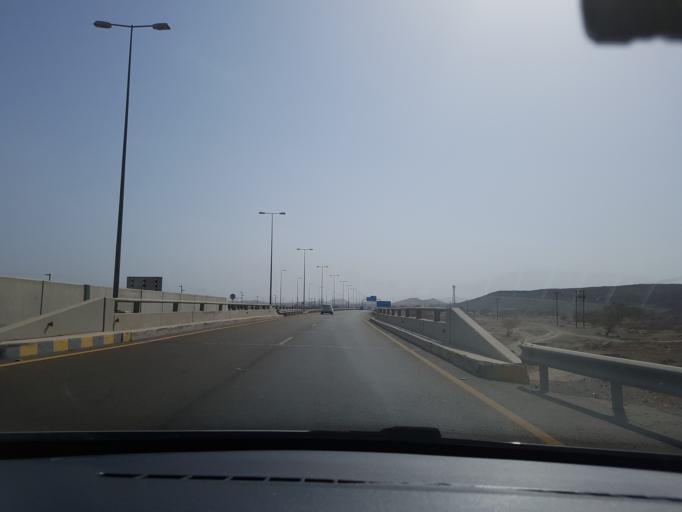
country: OM
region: Al Batinah
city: Al Liwa'
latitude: 24.3957
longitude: 56.5726
